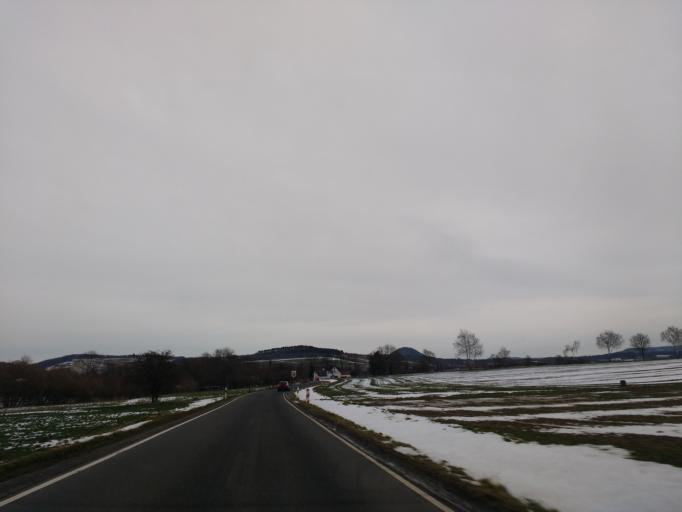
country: DE
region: Lower Saxony
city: Gemeinde Friedland
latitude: 51.3919
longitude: 9.9303
